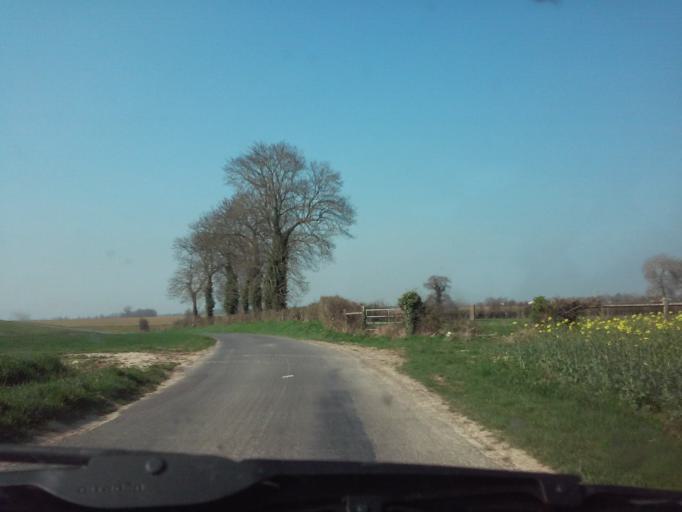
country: FR
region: Lower Normandy
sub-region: Departement du Calvados
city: Cheux
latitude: 49.1999
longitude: -0.5471
